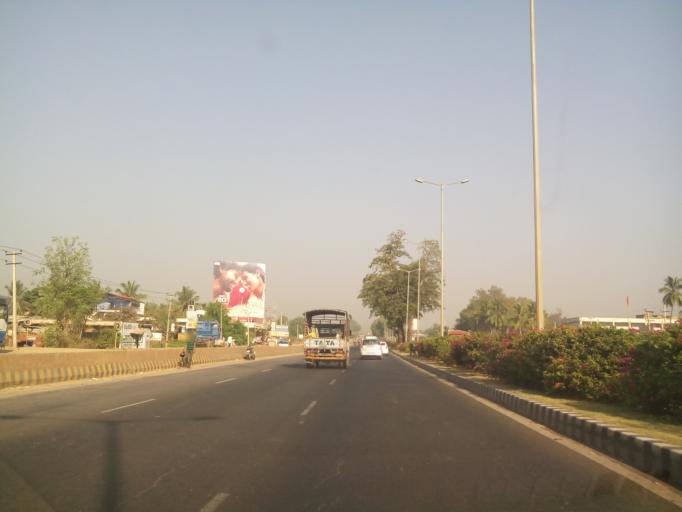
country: IN
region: Karnataka
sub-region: Bangalore Rural
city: Nelamangala
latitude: 13.0706
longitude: 77.4445
